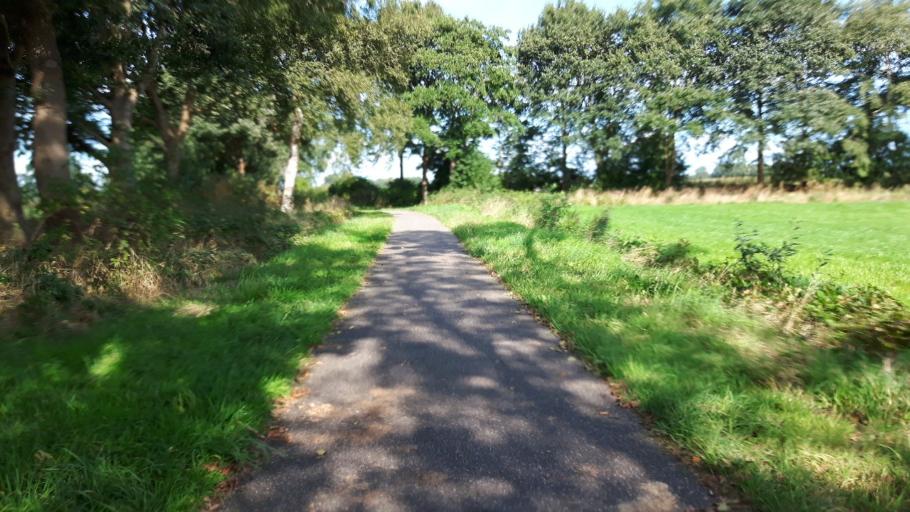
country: NL
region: Groningen
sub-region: Gemeente Leek
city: Leek
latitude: 53.1192
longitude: 6.4727
